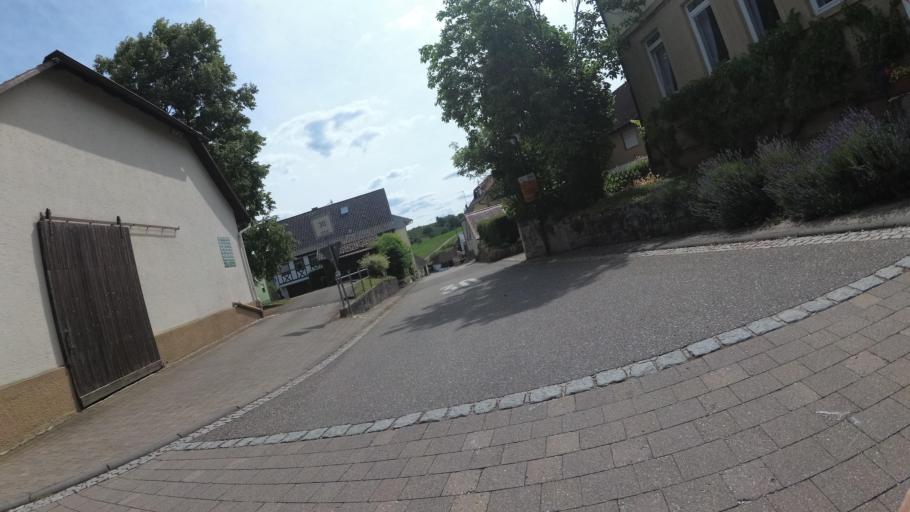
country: DE
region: Baden-Wuerttemberg
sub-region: Regierungsbezirk Stuttgart
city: Eberstadt
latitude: 49.1893
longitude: 9.3100
